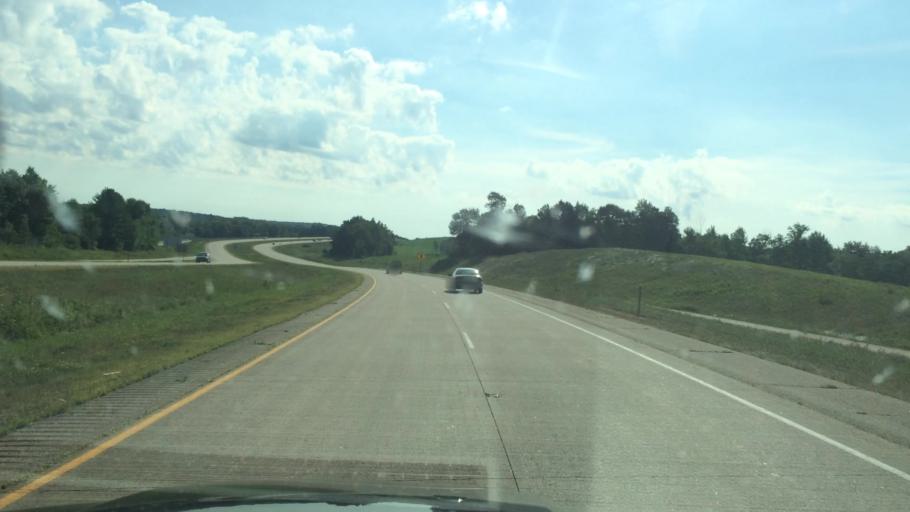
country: US
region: Wisconsin
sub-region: Shawano County
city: Wittenberg
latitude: 44.8239
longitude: -89.1211
